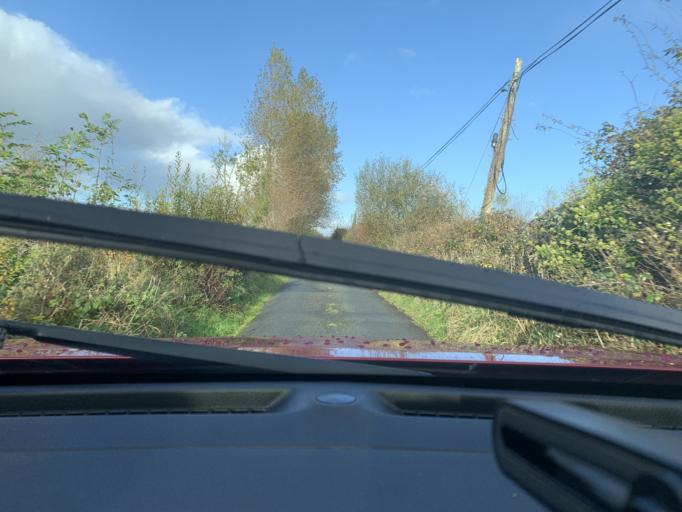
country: IE
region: Connaught
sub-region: Sligo
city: Ballymote
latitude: 54.0959
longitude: -8.4381
